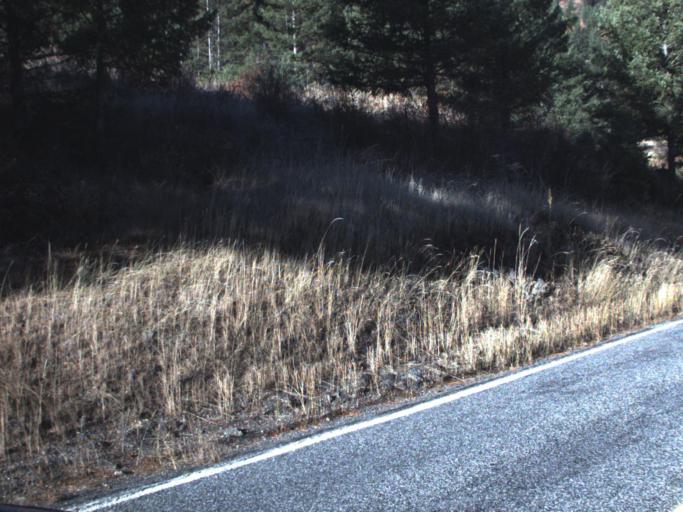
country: US
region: Washington
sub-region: Ferry County
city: Republic
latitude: 48.5638
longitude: -118.7449
